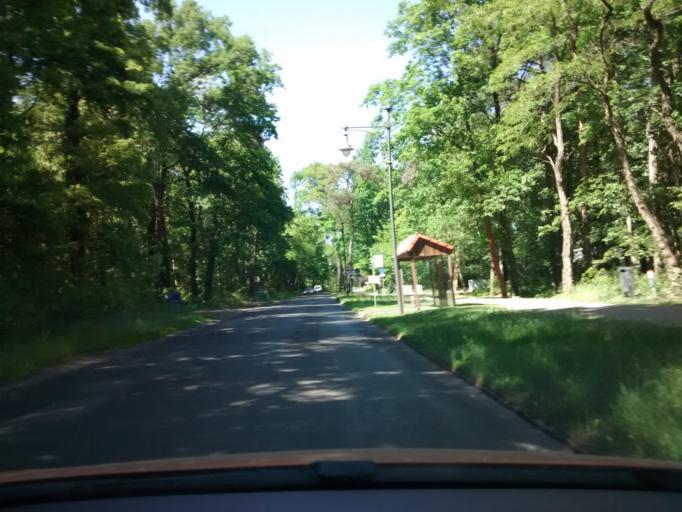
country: DE
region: Brandenburg
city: Bad Saarow
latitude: 52.2807
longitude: 14.0388
